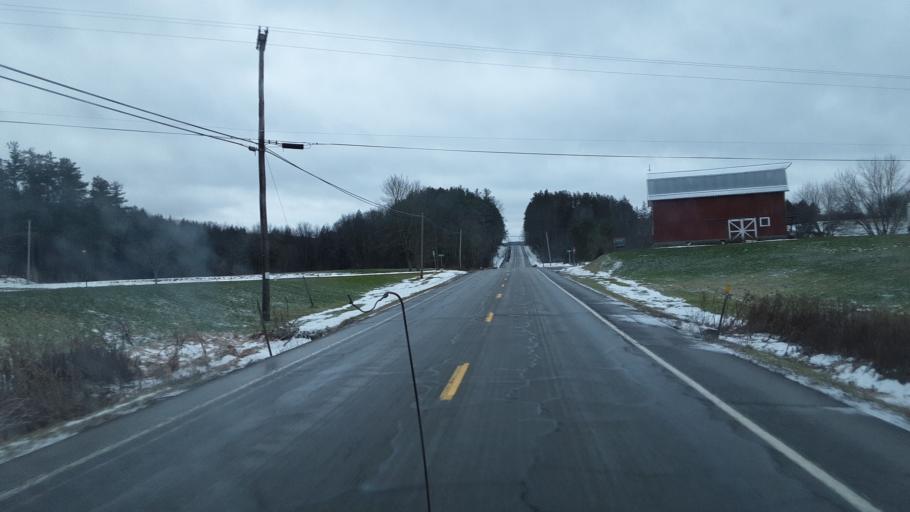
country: US
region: New York
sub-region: Allegany County
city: Friendship
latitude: 42.3151
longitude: -78.1294
